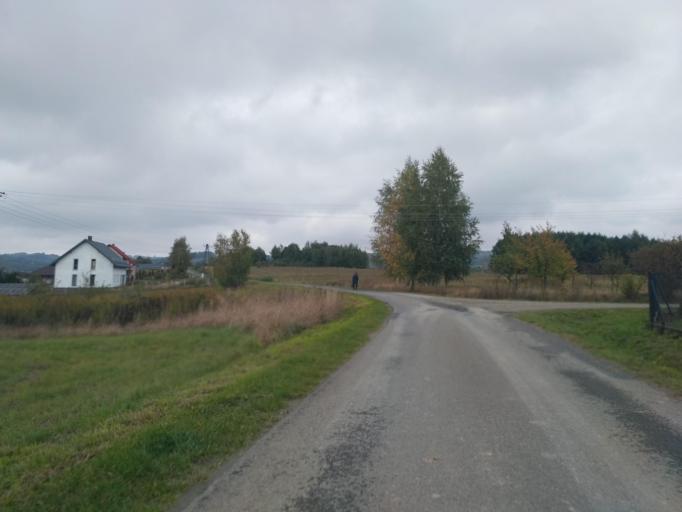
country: PL
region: Subcarpathian Voivodeship
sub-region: Powiat debicki
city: Brzostek
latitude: 49.9294
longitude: 21.4491
